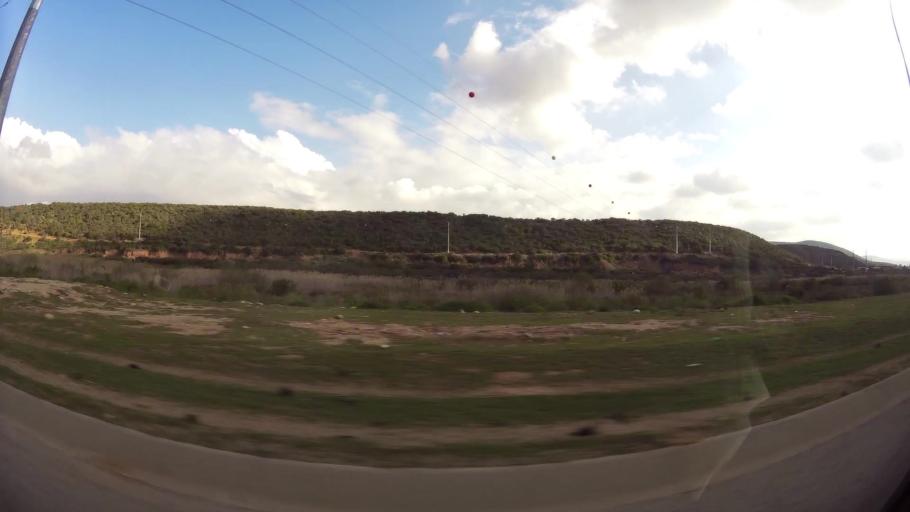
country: ZA
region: Eastern Cape
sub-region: Nelson Mandela Bay Metropolitan Municipality
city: Uitenhage
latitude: -33.7814
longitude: 25.3950
